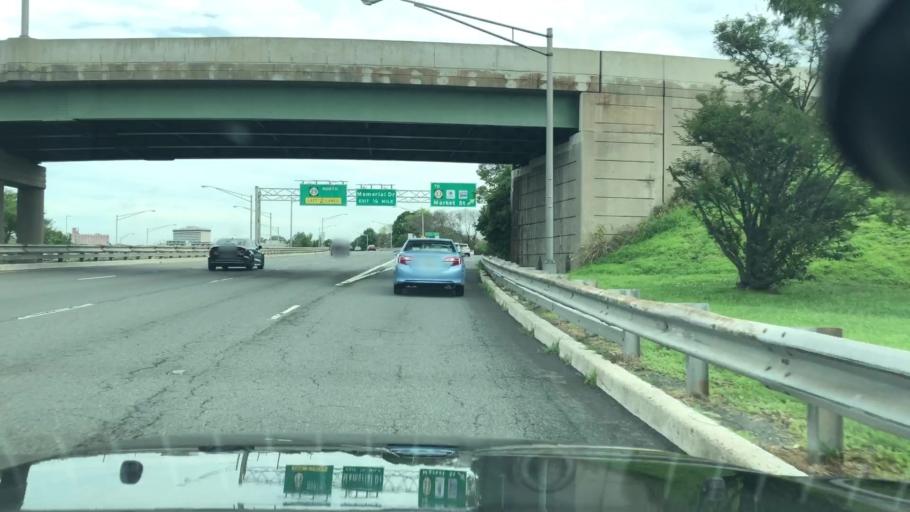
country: US
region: Pennsylvania
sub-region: Bucks County
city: Morrisville
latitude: 40.2113
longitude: -74.7667
